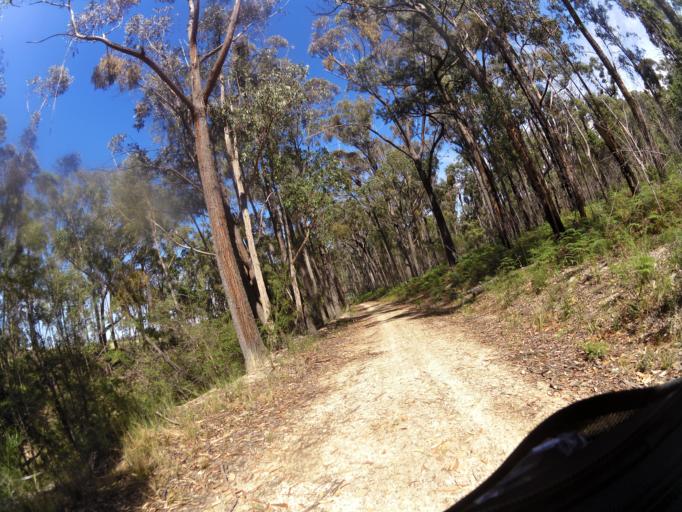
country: AU
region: Victoria
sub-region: East Gippsland
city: Lakes Entrance
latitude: -37.7175
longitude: 148.1338
